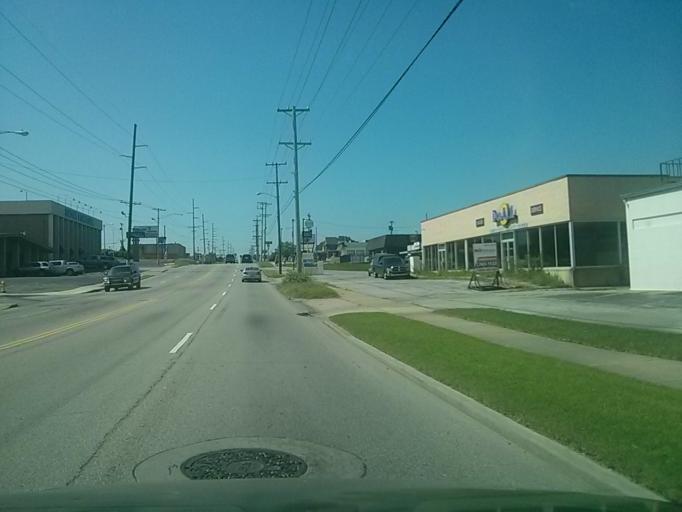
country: US
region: Oklahoma
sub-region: Tulsa County
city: Tulsa
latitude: 36.1510
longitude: -95.9046
